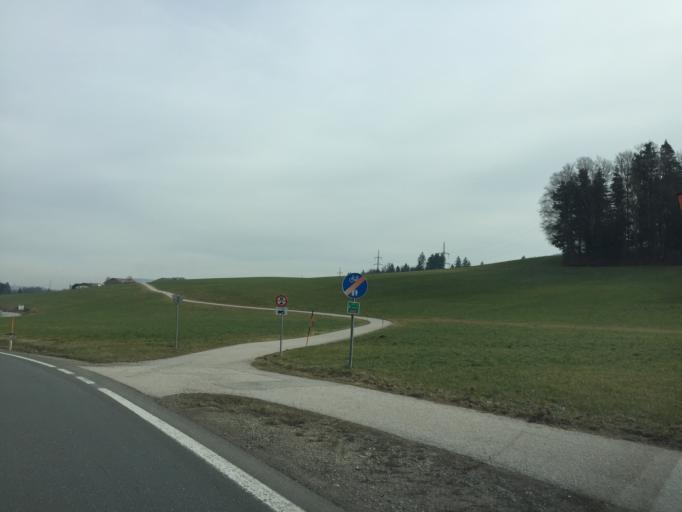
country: AT
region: Salzburg
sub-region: Politischer Bezirk Salzburg-Umgebung
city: Henndorf am Wallersee
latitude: 47.8816
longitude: 13.1723
